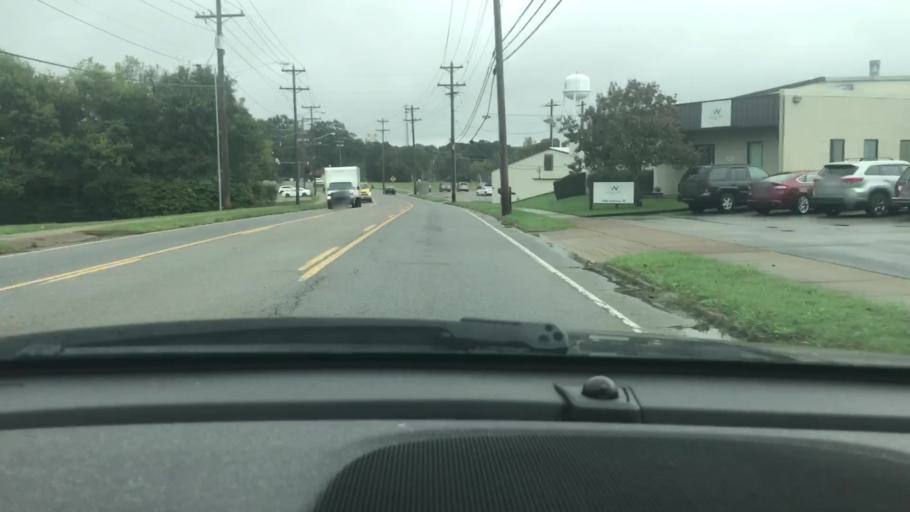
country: US
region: Tennessee
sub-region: Dickson County
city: White Bluff
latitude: 36.1058
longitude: -87.2178
